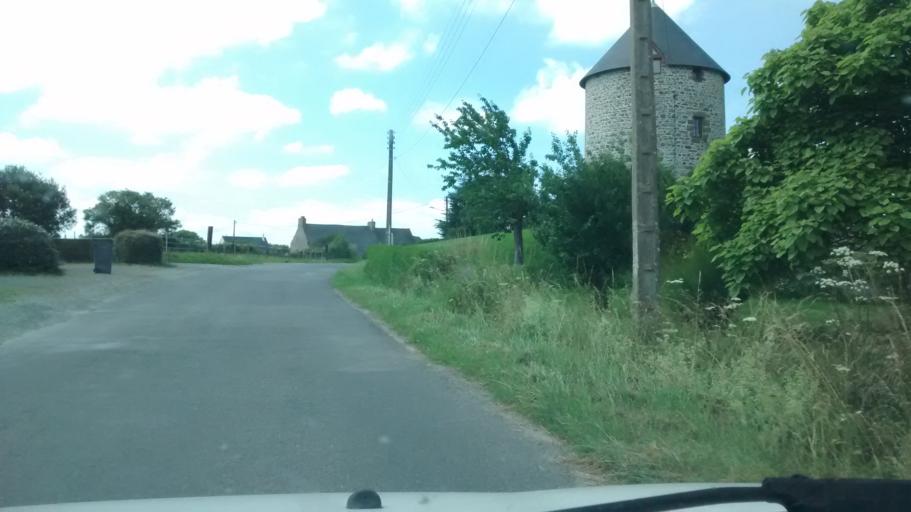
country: FR
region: Brittany
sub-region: Departement d'Ille-et-Vilaine
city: La Gouesniere
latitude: 48.5949
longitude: -1.8981
